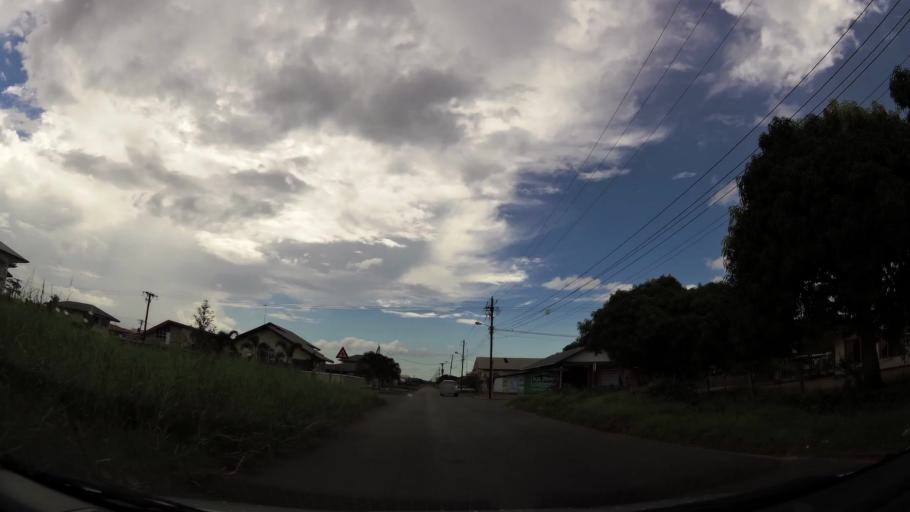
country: SR
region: Paramaribo
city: Paramaribo
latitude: 5.8455
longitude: -55.1289
